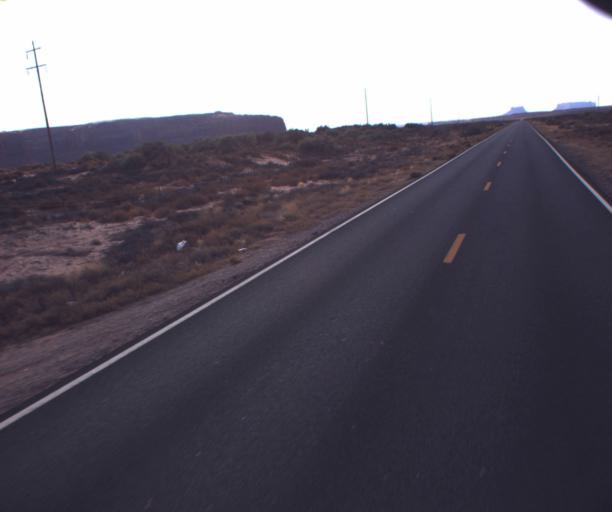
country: US
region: Arizona
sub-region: Apache County
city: Many Farms
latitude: 36.6437
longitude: -109.5897
